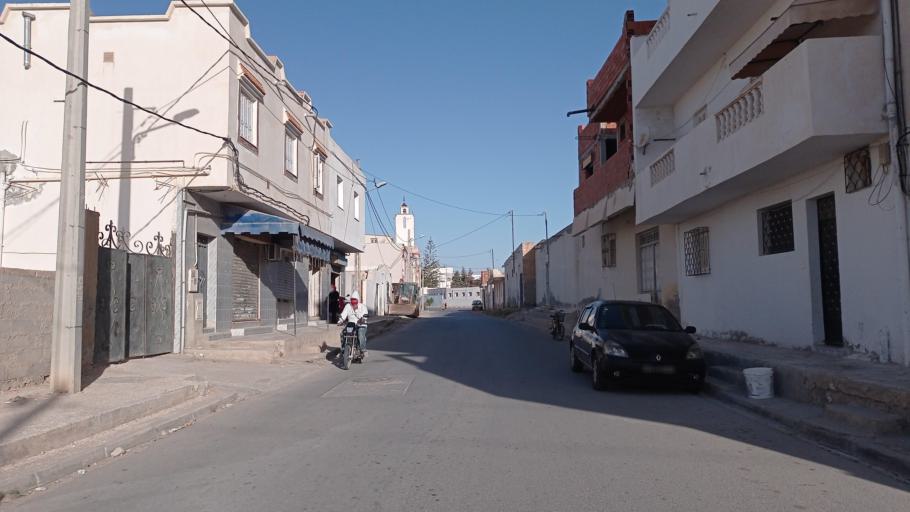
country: TN
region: Qabis
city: Gabes
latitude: 33.8587
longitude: 10.1173
